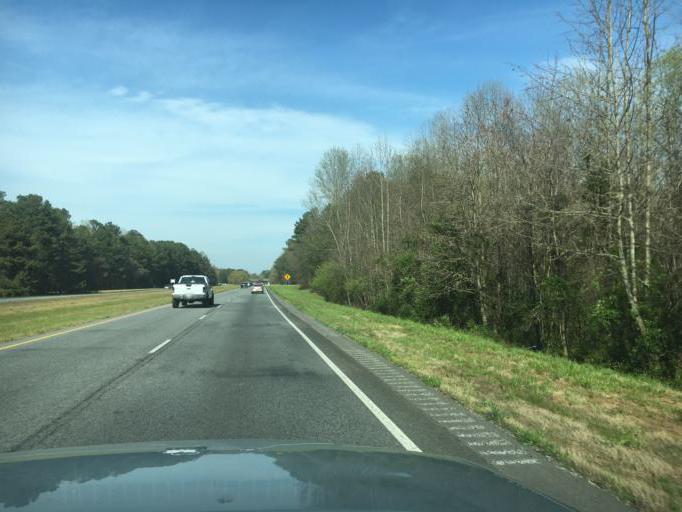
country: US
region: Georgia
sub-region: Habersham County
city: Cornelia
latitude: 34.5151
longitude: -83.5535
